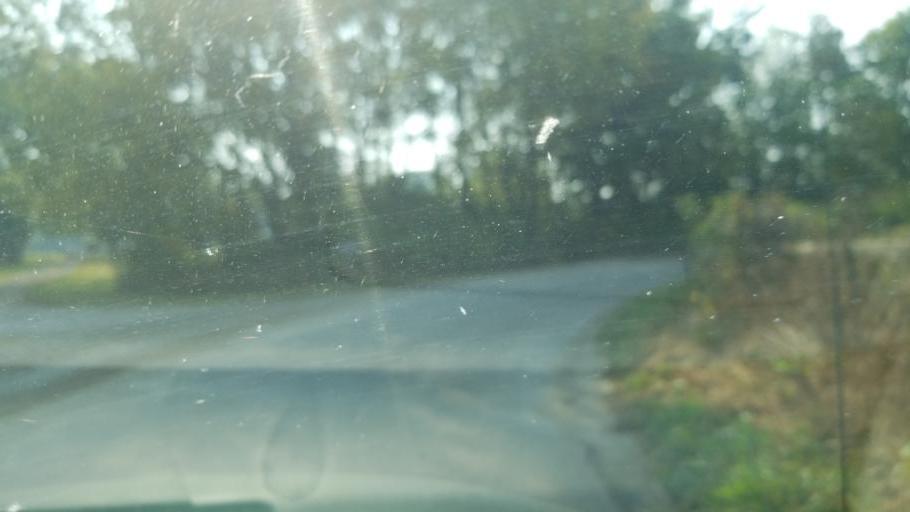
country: US
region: Ohio
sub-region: Knox County
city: Centerburg
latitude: 40.2749
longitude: -82.5853
